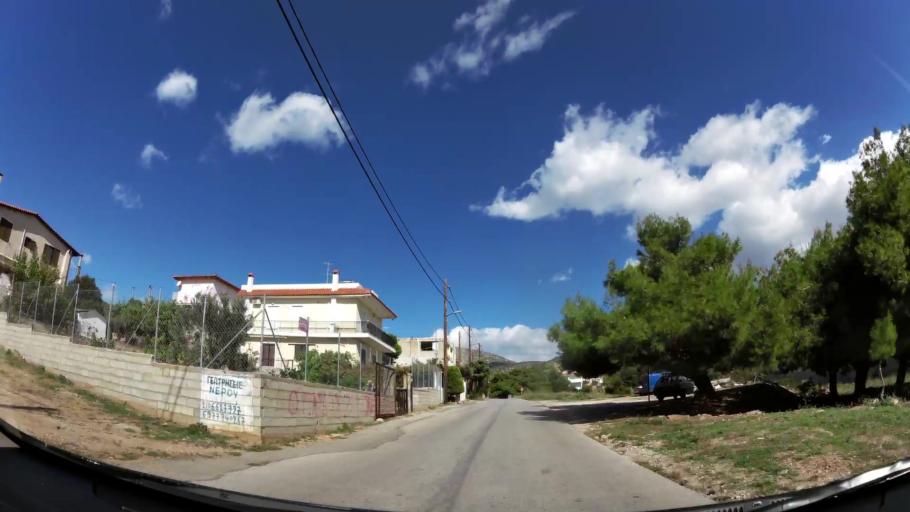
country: GR
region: Attica
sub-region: Nomarchia Anatolikis Attikis
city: Vari
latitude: 37.8407
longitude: 23.7963
